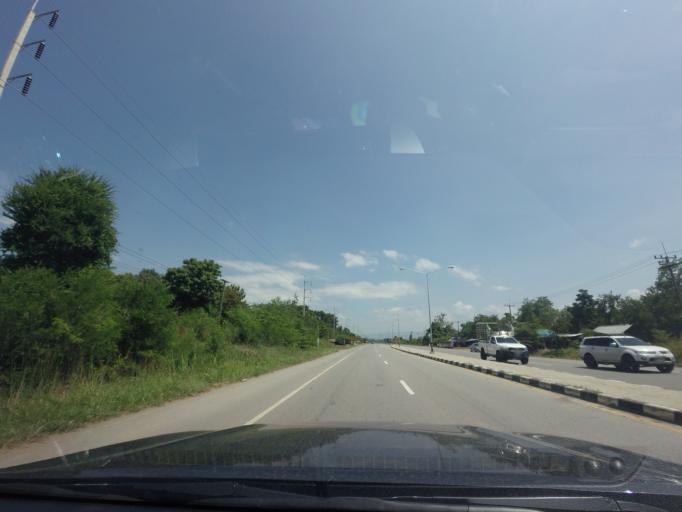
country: TH
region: Phetchabun
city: Lom Sak
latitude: 16.7674
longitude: 101.1627
